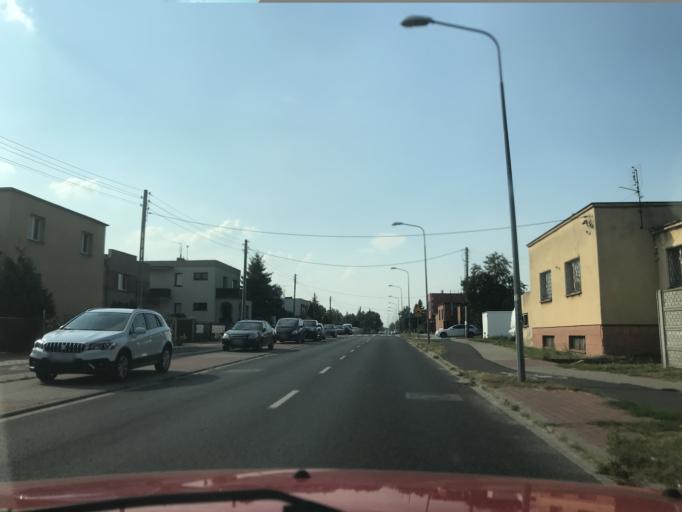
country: PL
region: Greater Poland Voivodeship
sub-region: Powiat poznanski
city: Plewiska
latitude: 52.3801
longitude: 16.8200
